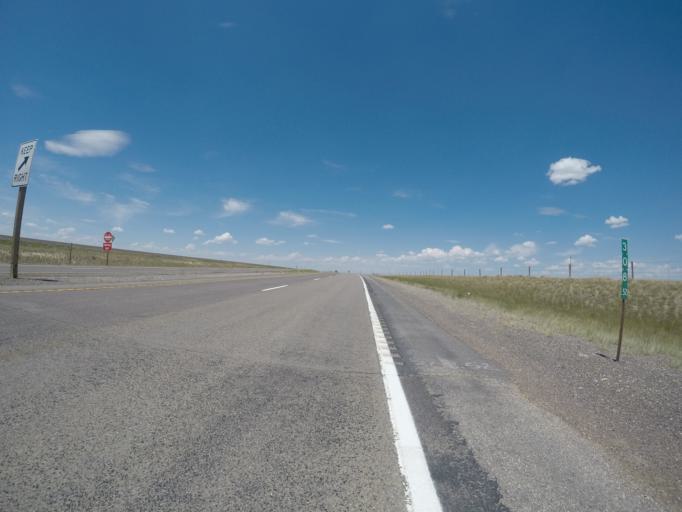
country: US
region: Wyoming
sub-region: Albany County
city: Laramie
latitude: 41.5830
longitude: -105.6994
